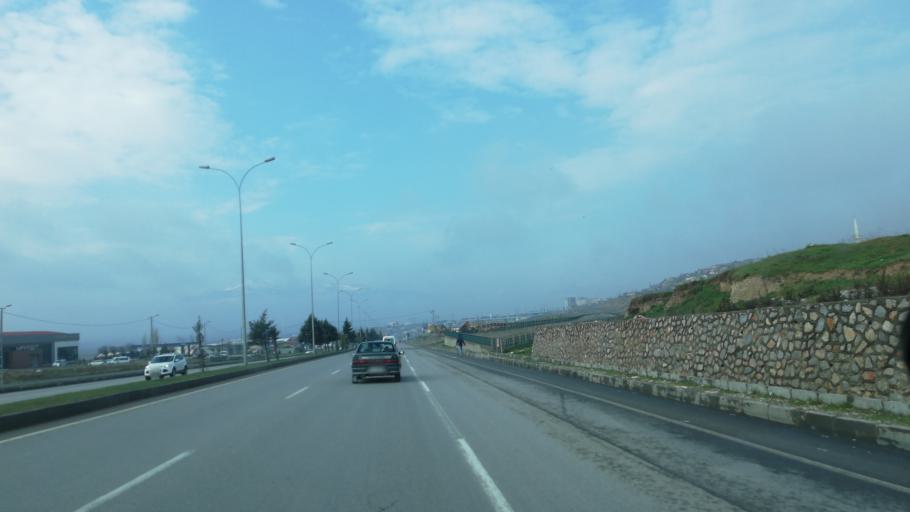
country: TR
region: Kahramanmaras
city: Kahramanmaras
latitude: 37.5670
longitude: 36.9063
